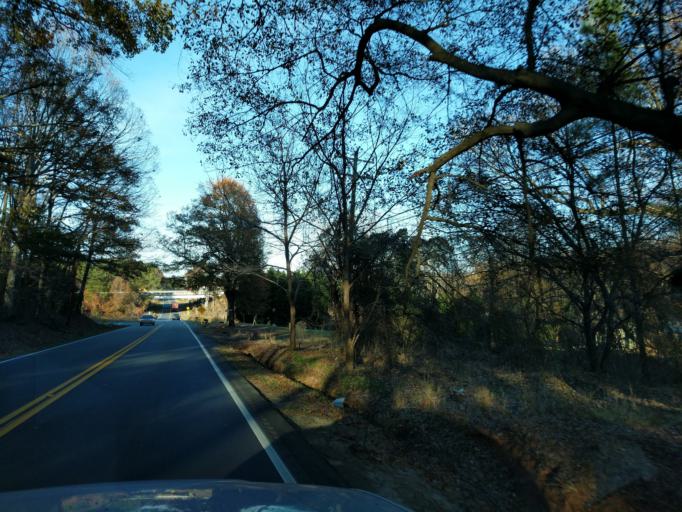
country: US
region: South Carolina
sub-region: Spartanburg County
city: Valley Falls
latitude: 35.0098
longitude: -81.9511
